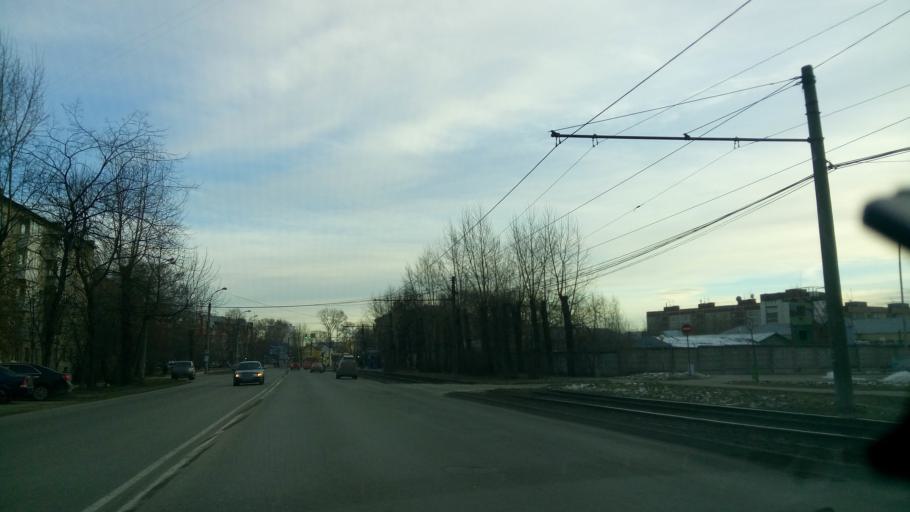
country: RU
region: Sverdlovsk
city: Shuvakish
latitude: 56.8751
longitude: 60.5161
